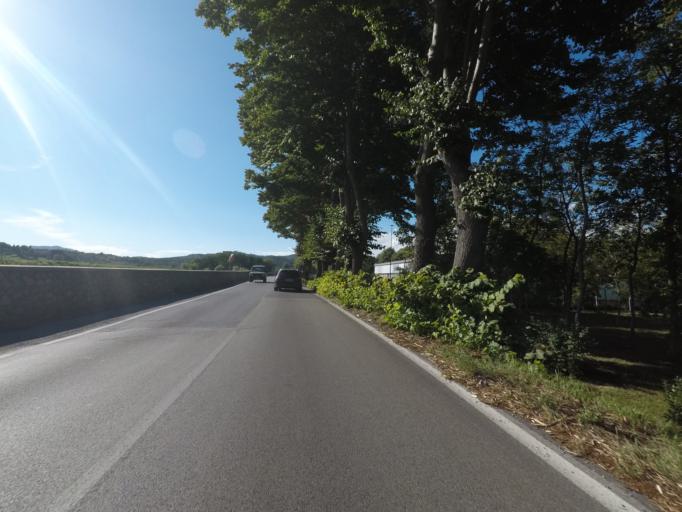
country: IT
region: Tuscany
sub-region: Provincia di Lucca
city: Lucca
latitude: 43.8707
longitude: 10.5003
